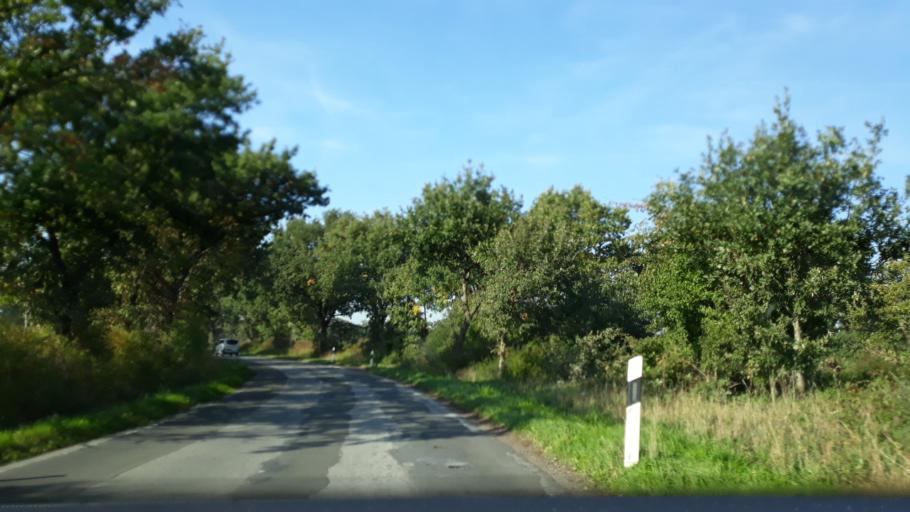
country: DE
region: Schleswig-Holstein
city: Borm
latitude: 54.3981
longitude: 9.3989
